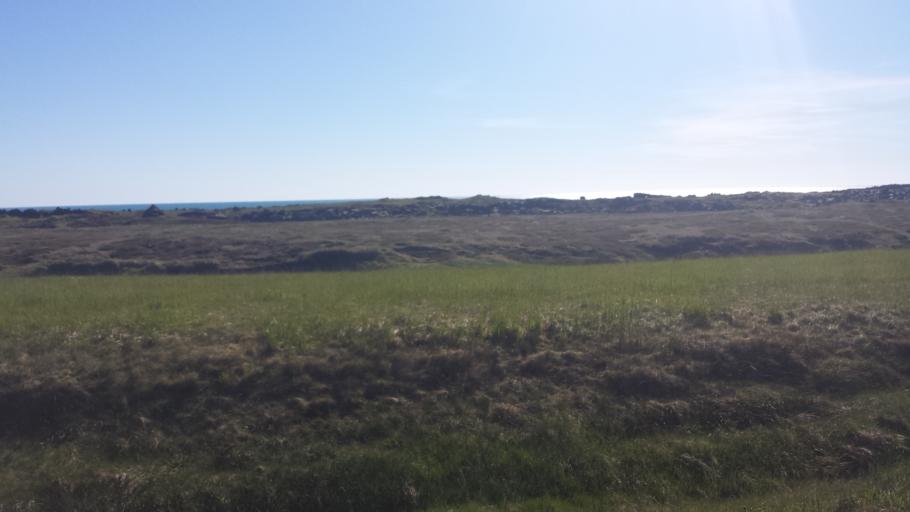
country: IS
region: West
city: Olafsvik
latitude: 64.7300
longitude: -23.8027
